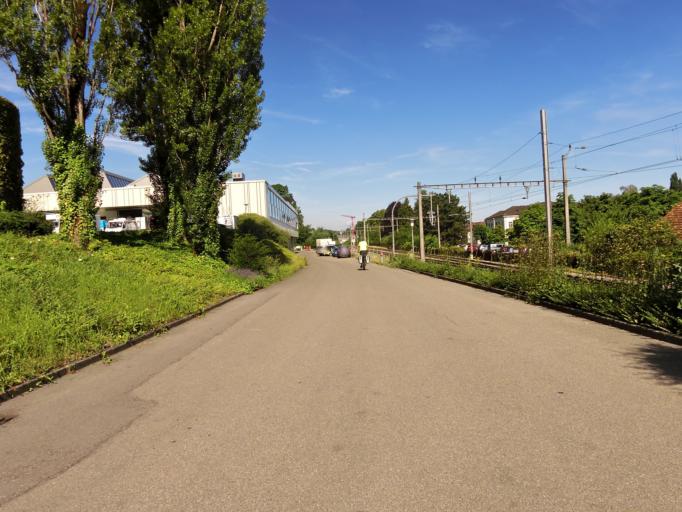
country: CH
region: Thurgau
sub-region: Kreuzlingen District
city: Munsterlingen
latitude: 47.6326
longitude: 9.2324
